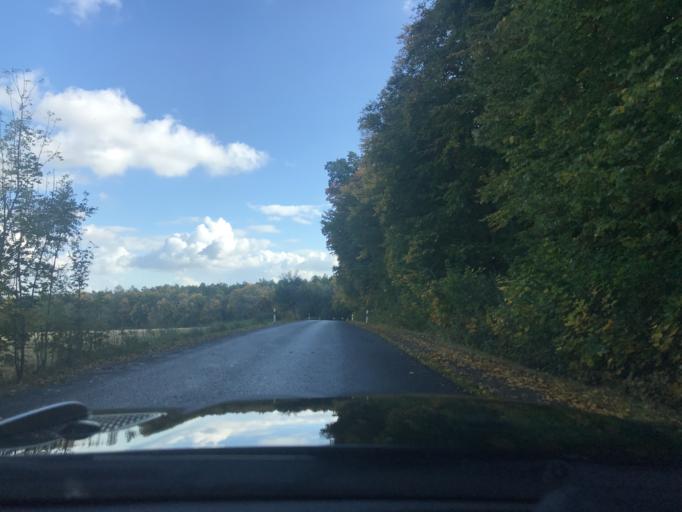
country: DE
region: Thuringia
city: Oberdorla
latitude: 51.1869
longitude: 10.3957
